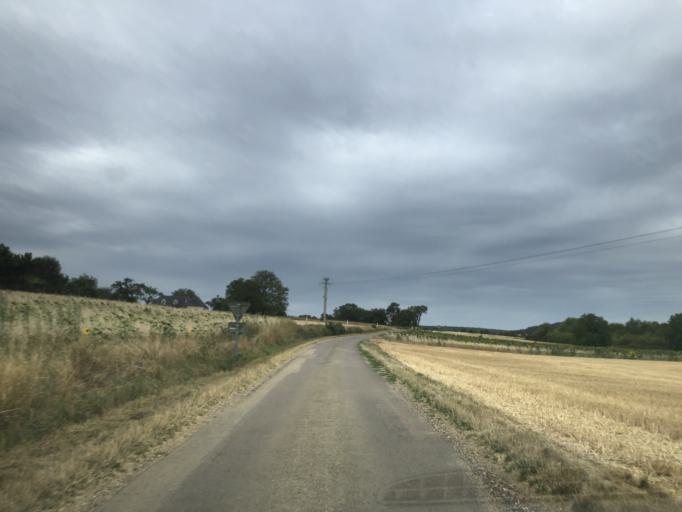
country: FR
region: Bourgogne
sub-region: Departement de l'Yonne
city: Aillant-sur-Tholon
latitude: 47.9129
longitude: 3.3464
